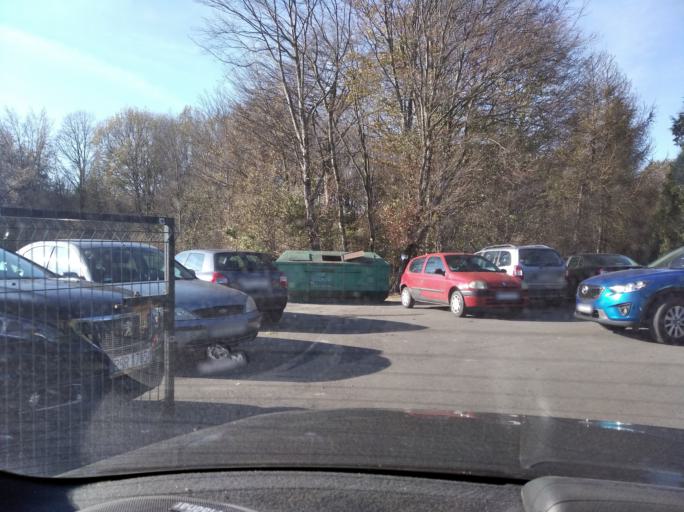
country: PL
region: Subcarpathian Voivodeship
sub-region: Powiat ropczycko-sedziszowski
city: Wielopole Skrzynskie
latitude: 49.9264
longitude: 21.5569
